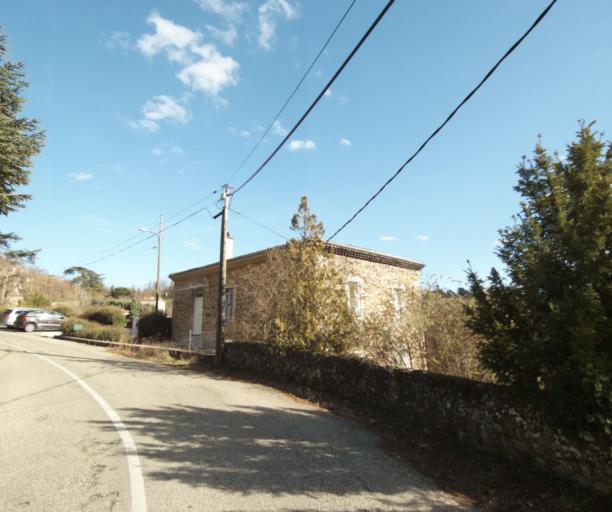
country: FR
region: Rhone-Alpes
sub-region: Departement de l'Ardeche
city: Annonay
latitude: 45.2532
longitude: 4.6787
